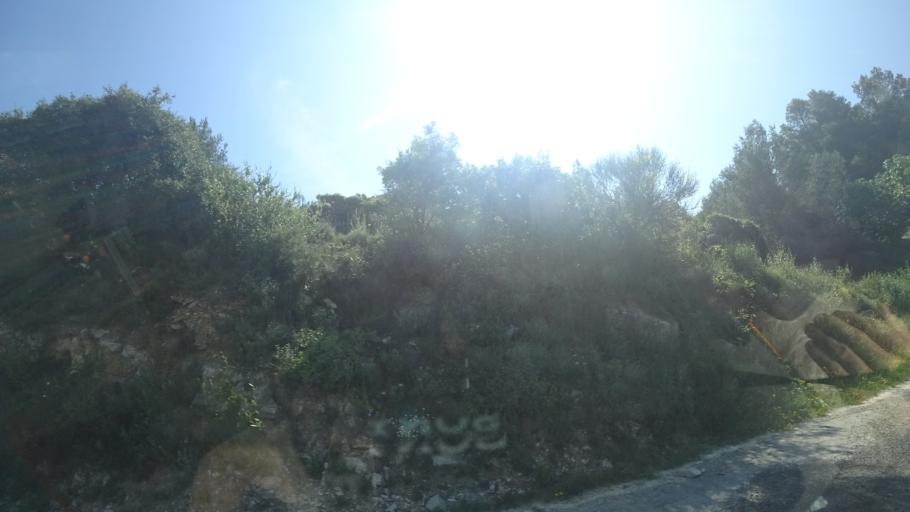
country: FR
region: Languedoc-Roussillon
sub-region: Departement de l'Herault
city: Olonzac
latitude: 43.3500
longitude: 2.7417
